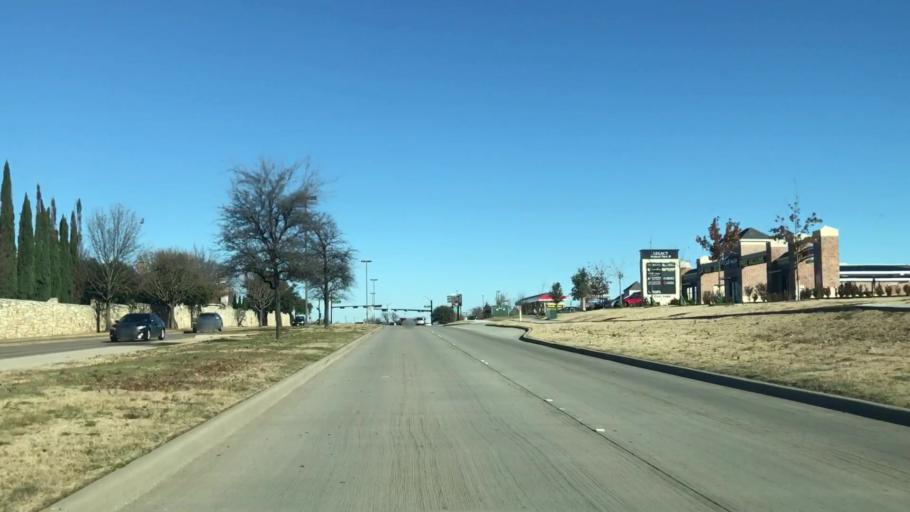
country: US
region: Texas
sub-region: Denton County
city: The Colony
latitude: 33.1044
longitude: -96.8415
